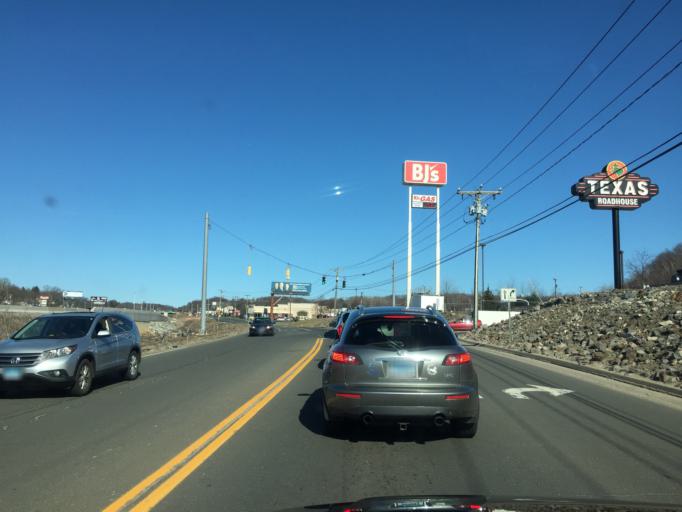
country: US
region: Connecticut
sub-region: New Haven County
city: Prospect
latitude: 41.5376
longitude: -73.0032
